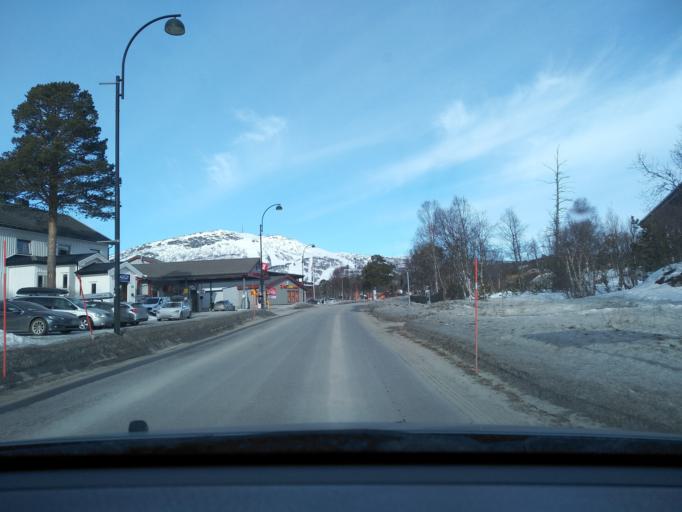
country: NO
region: Aust-Agder
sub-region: Bykle
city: Hovden
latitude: 59.5588
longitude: 7.3572
